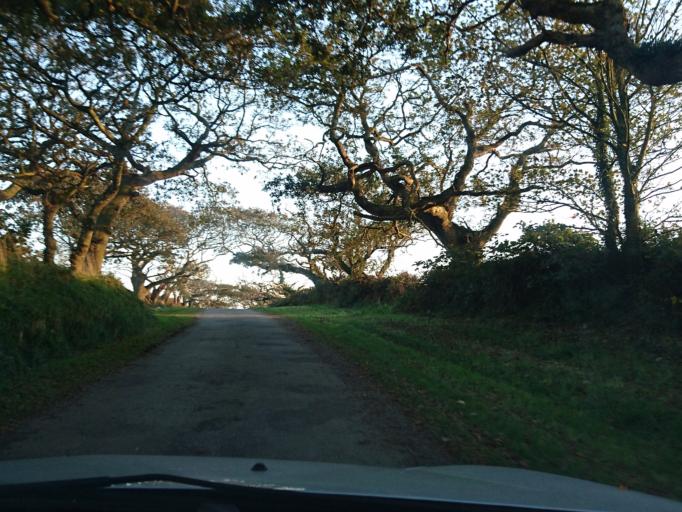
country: FR
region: Brittany
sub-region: Departement du Finistere
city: Lanrivoare
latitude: 48.4745
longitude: -4.6659
